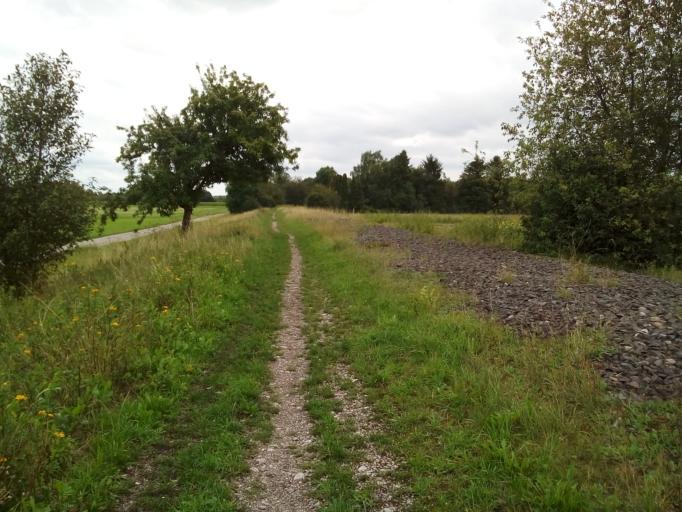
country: DE
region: Bavaria
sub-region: Upper Bavaria
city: Unterfoehring
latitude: 48.1674
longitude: 11.6722
